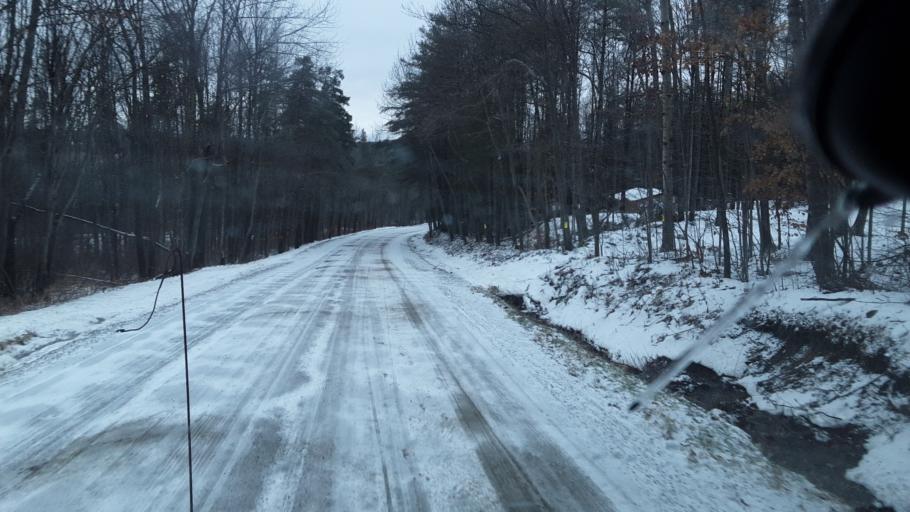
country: US
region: New York
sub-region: Allegany County
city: Friendship
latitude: 42.2824
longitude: -78.1622
